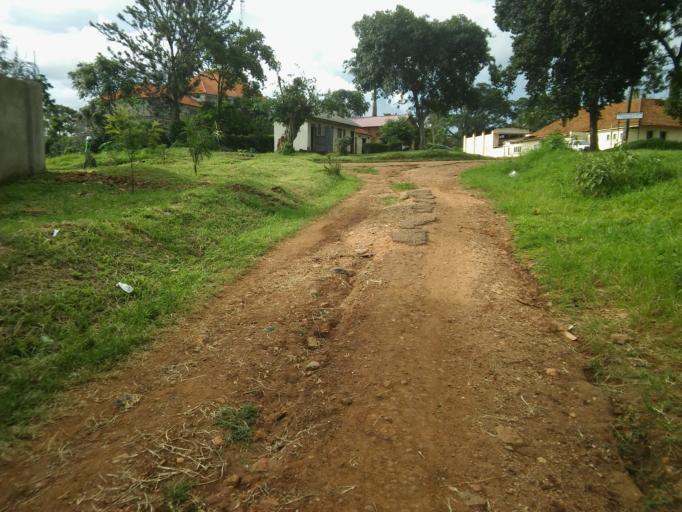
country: UG
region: Eastern Region
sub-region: Mbale District
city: Mbale
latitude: 1.0674
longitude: 34.1851
